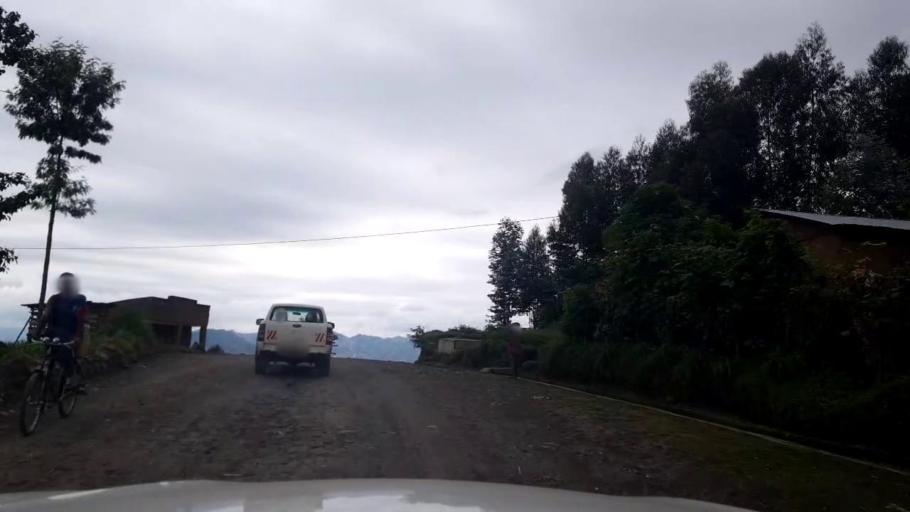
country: RW
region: Northern Province
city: Musanze
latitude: -1.4996
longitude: 29.5340
